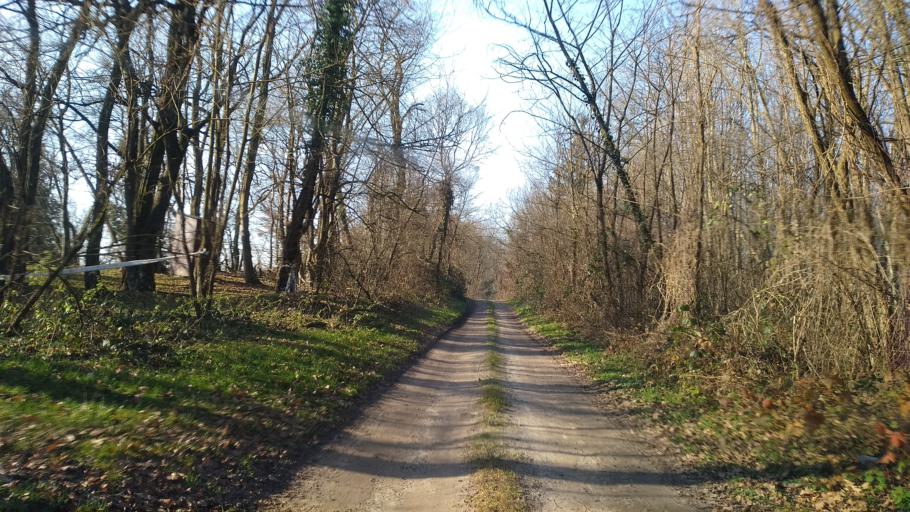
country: HU
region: Somogy
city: Barcs
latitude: 45.9521
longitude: 17.5202
